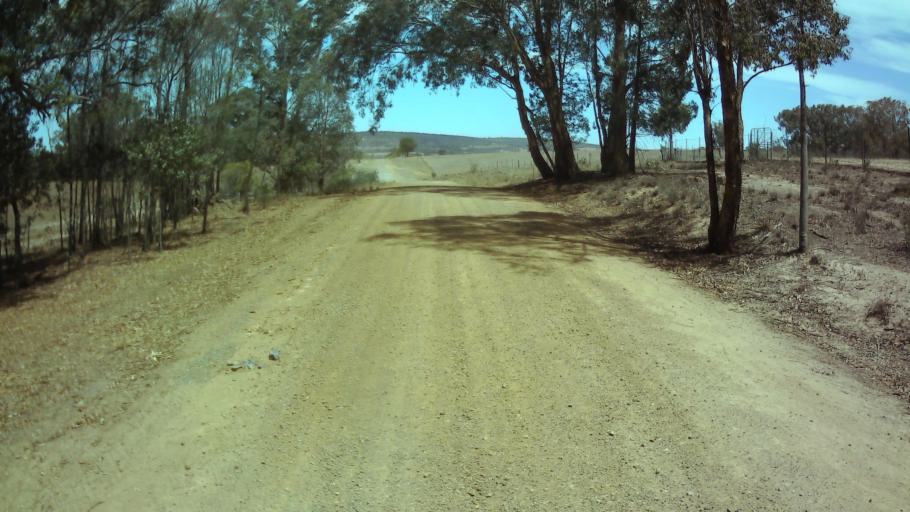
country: AU
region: New South Wales
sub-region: Weddin
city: Grenfell
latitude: -33.8203
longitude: 148.1674
